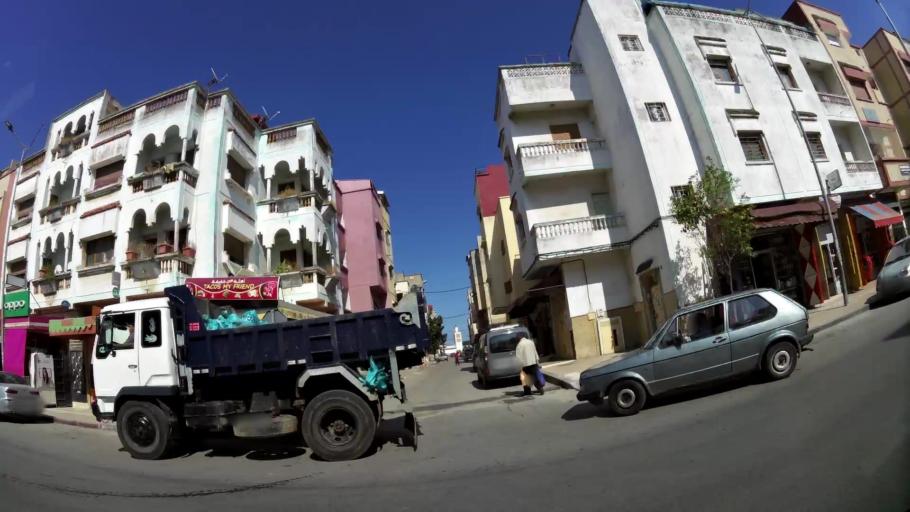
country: MA
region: Rabat-Sale-Zemmour-Zaer
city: Sale
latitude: 34.0459
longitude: -6.7786
